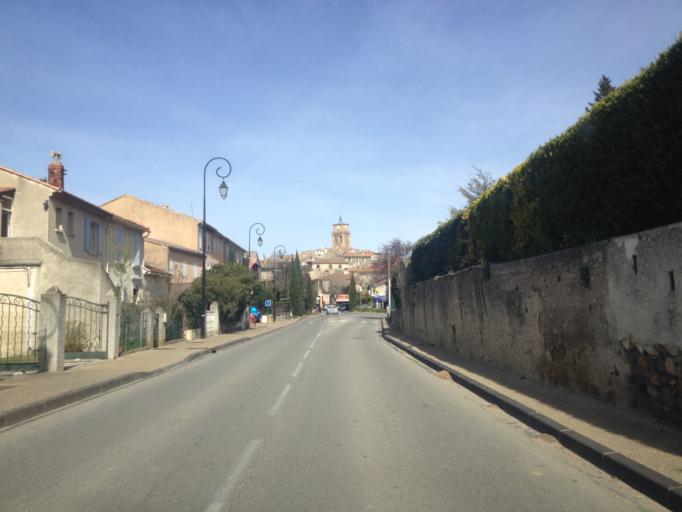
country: FR
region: Provence-Alpes-Cote d'Azur
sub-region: Departement du Vaucluse
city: Sablet
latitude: 44.1900
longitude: 5.0085
